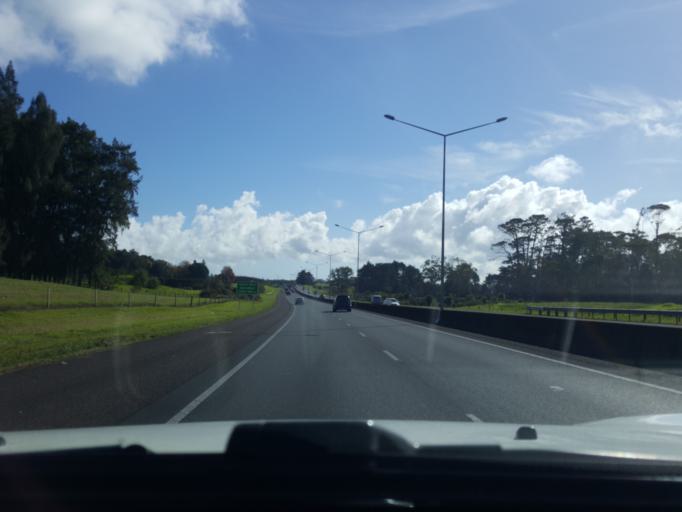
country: NZ
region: Auckland
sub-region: Auckland
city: Rosebank
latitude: -36.8027
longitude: 174.6031
